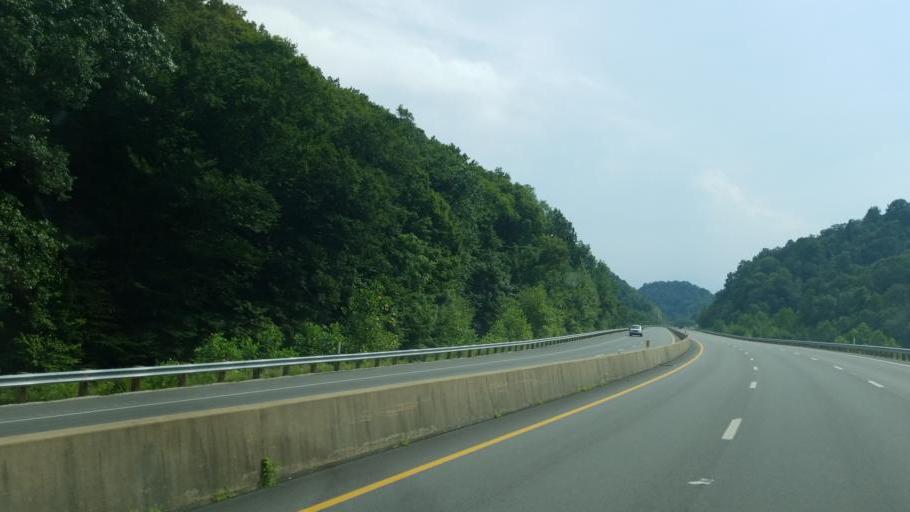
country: US
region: West Virginia
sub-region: Logan County
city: Chapmanville
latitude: 37.9252
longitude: -82.0303
